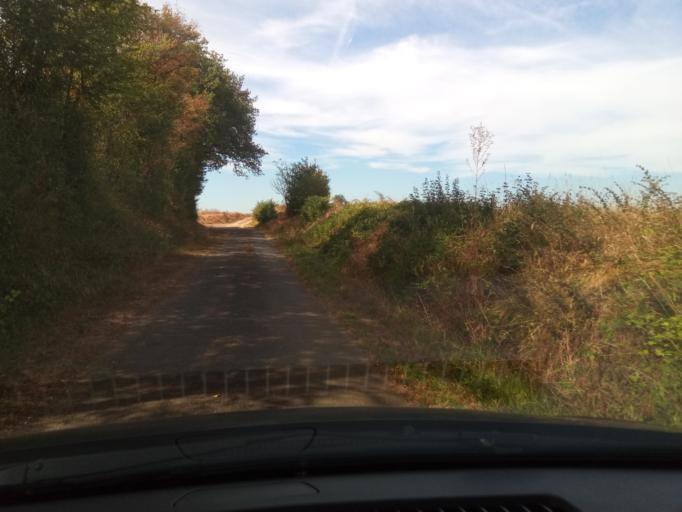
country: FR
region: Poitou-Charentes
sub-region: Departement de la Vienne
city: Chauvigny
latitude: 46.5564
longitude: 0.7423
